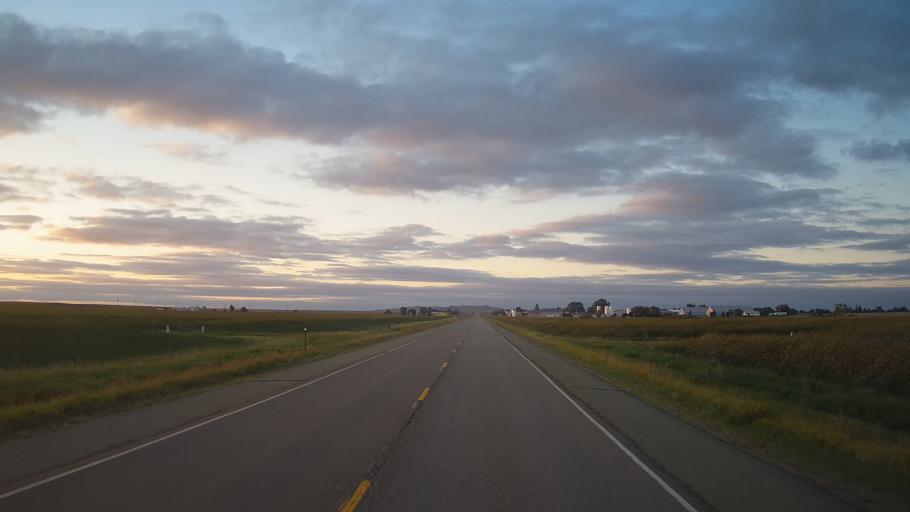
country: US
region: South Dakota
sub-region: Lyman County
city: Kennebec
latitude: 43.8689
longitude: -99.6061
